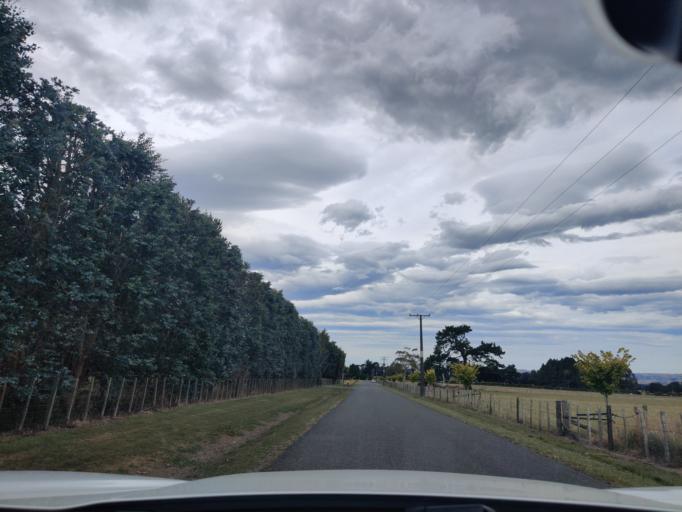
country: NZ
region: Wellington
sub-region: Masterton District
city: Masterton
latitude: -41.0365
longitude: 175.4408
